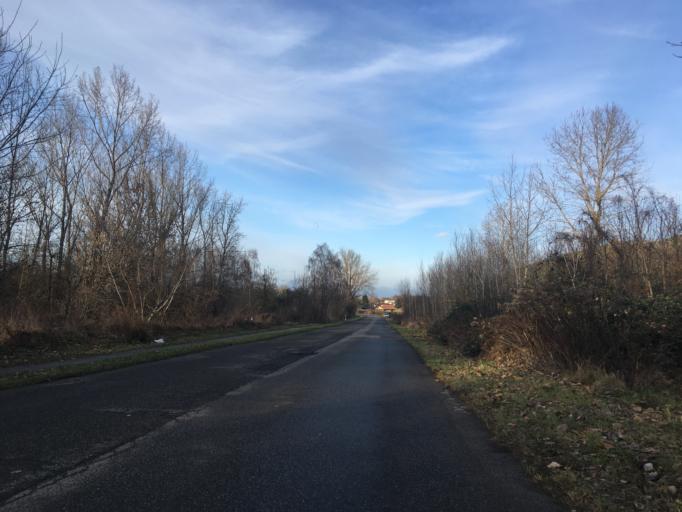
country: DE
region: Berlin
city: Blankenfelde
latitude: 52.6359
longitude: 13.4010
